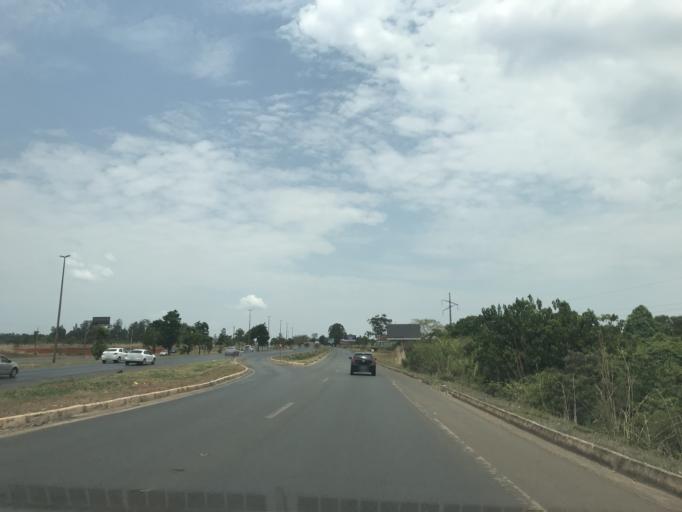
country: BR
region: Federal District
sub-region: Brasilia
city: Brasilia
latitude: -15.6662
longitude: -47.8097
